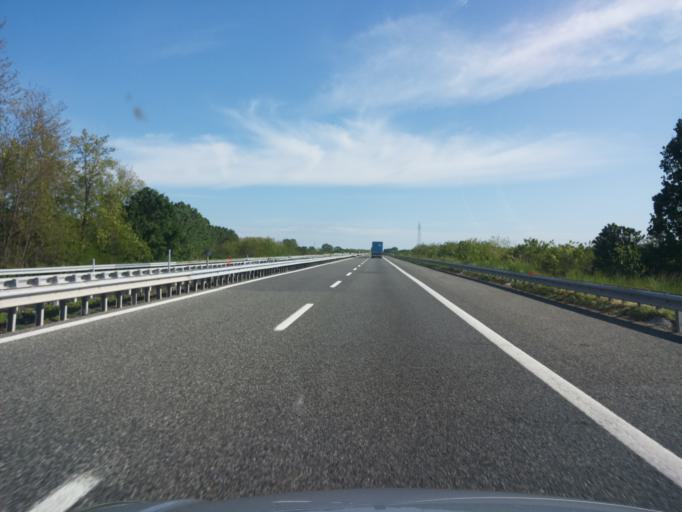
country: IT
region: Piedmont
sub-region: Provincia di Novara
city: Carpignano Sesia
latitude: 45.5452
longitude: 8.4255
